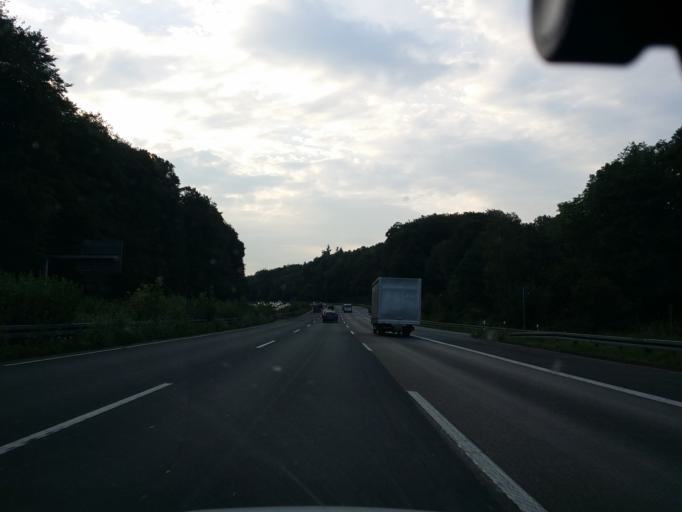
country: DE
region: Hesse
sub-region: Regierungsbezirk Darmstadt
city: Niedernhausen
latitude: 50.1460
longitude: 8.3256
